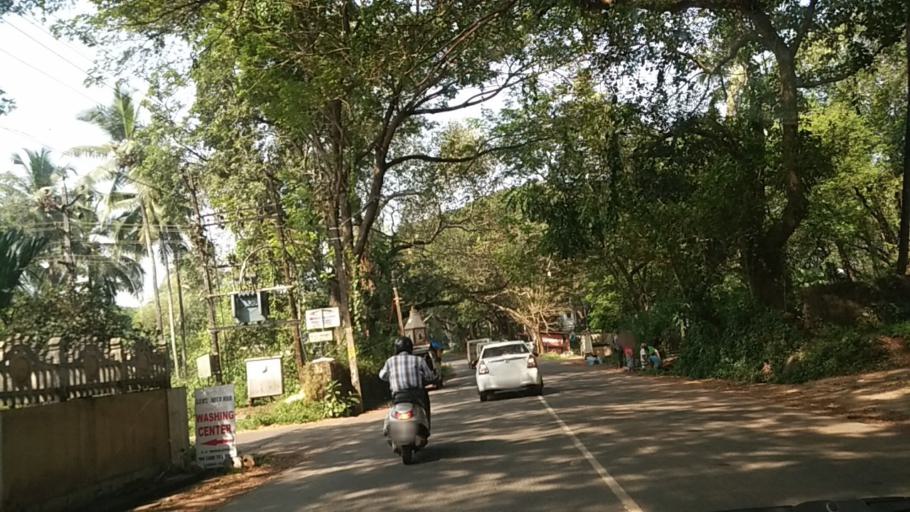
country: IN
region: Goa
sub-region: North Goa
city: Jua
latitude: 15.5004
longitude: 73.9019
